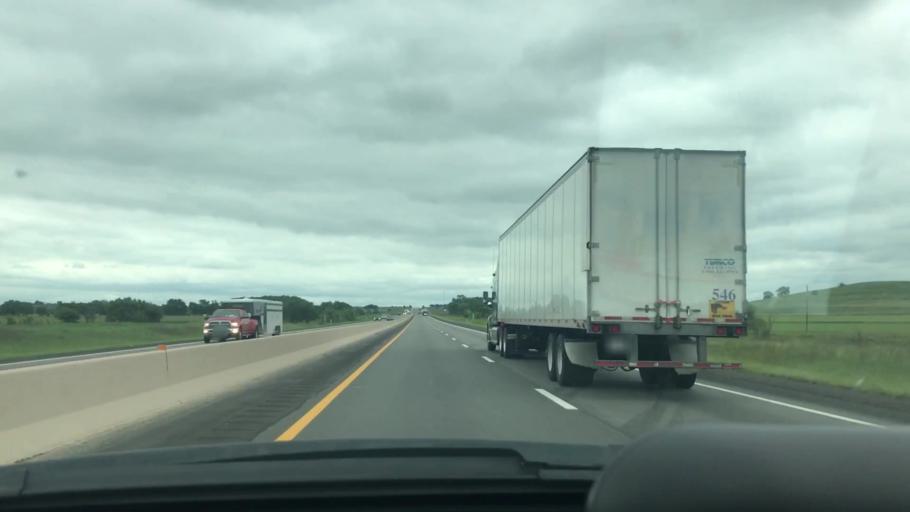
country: US
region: Oklahoma
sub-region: Ottawa County
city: Afton
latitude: 36.6830
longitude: -95.0357
